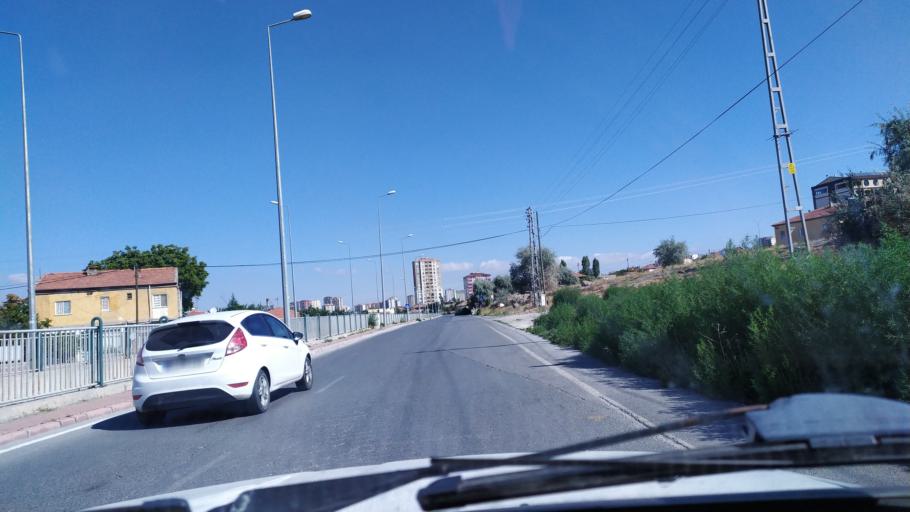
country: TR
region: Kayseri
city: Talas
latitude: 38.7239
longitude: 35.5505
